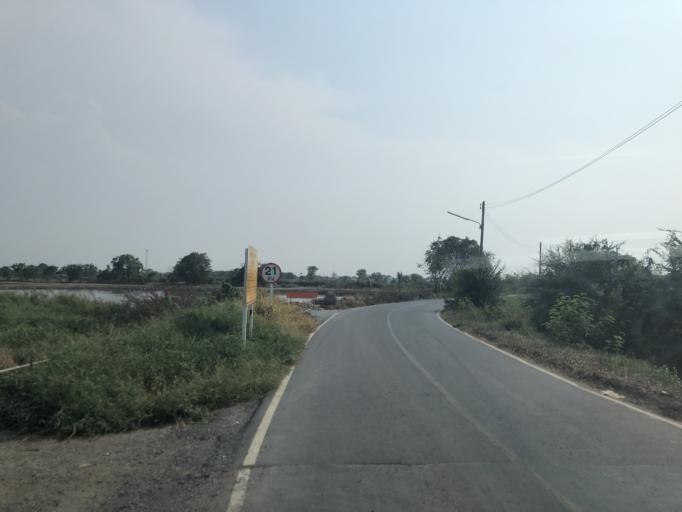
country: TH
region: Chachoengsao
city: Bang Pakong
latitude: 13.5170
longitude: 100.9248
